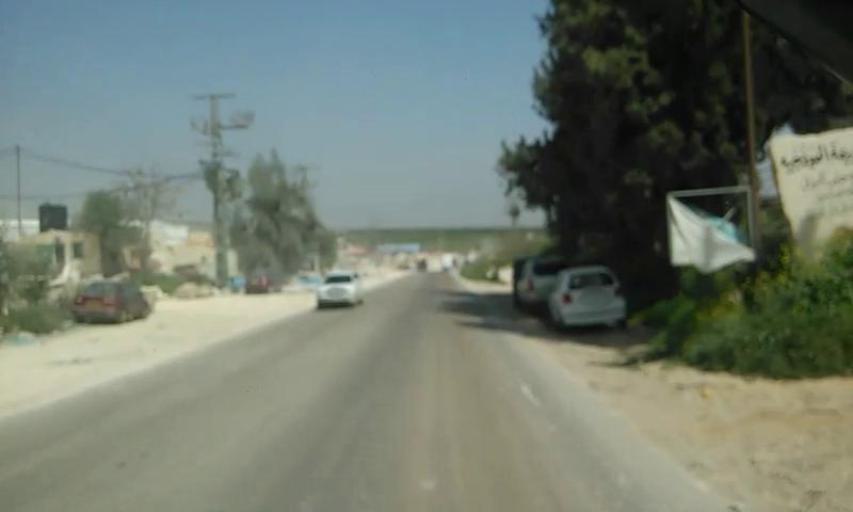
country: PS
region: West Bank
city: Ash Shuhada'
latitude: 32.4362
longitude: 35.2723
